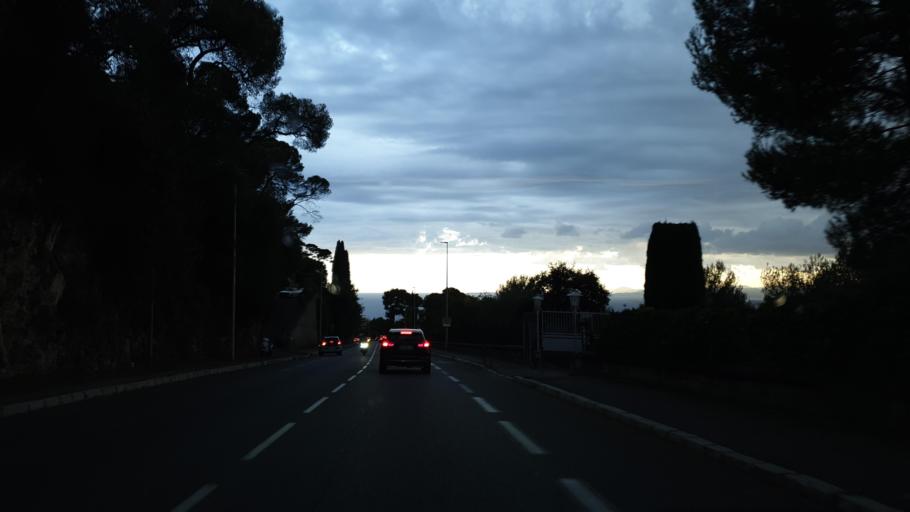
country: FR
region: Provence-Alpes-Cote d'Azur
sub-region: Departement des Alpes-Maritimes
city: Villefranche-sur-Mer
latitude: 43.7023
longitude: 7.2977
